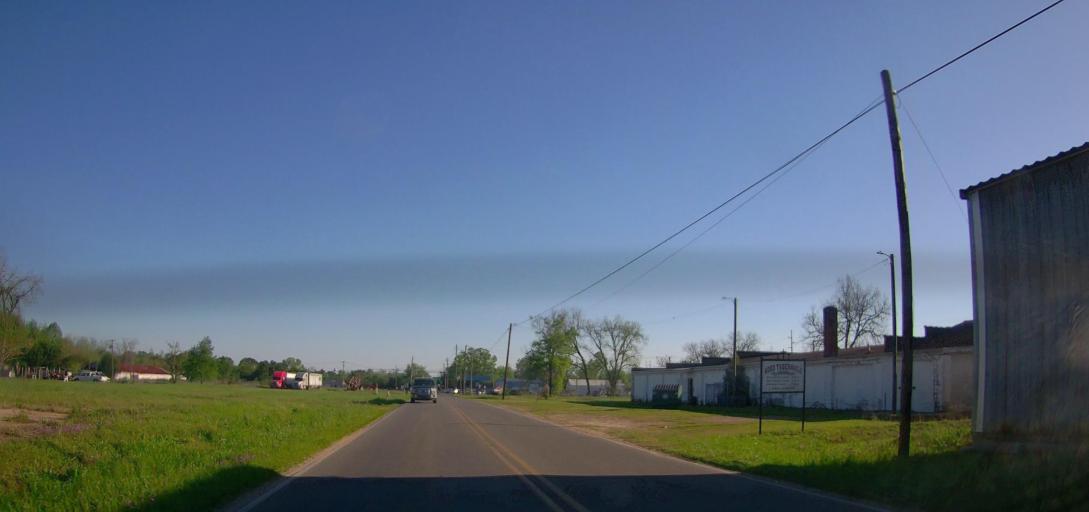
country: US
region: Georgia
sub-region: Ben Hill County
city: Fitzgerald
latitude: 31.7166
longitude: -83.2441
